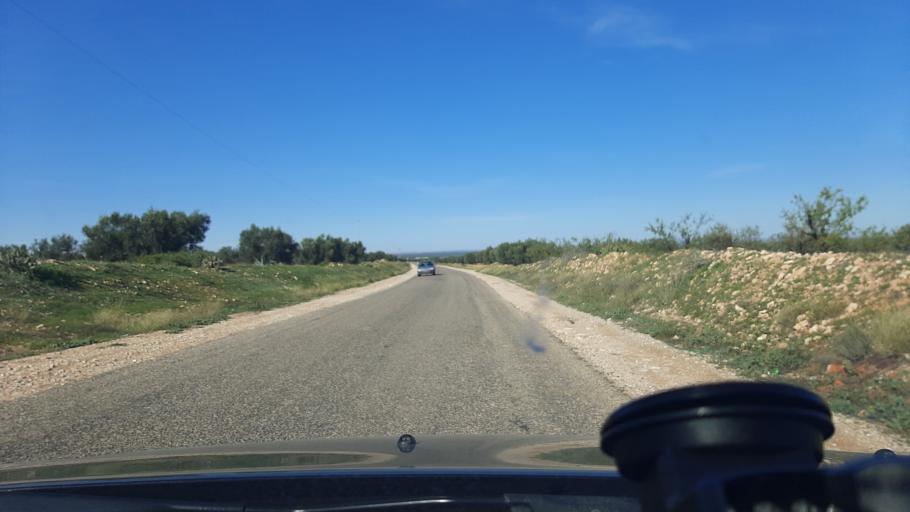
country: TN
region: Safaqis
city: Sfax
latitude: 34.9596
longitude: 10.5431
